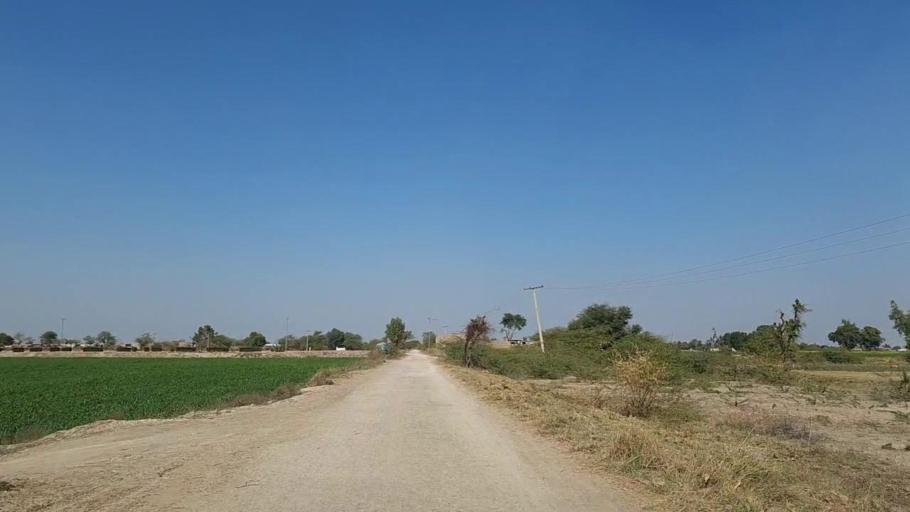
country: PK
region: Sindh
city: Nawabshah
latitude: 26.2522
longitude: 68.4411
